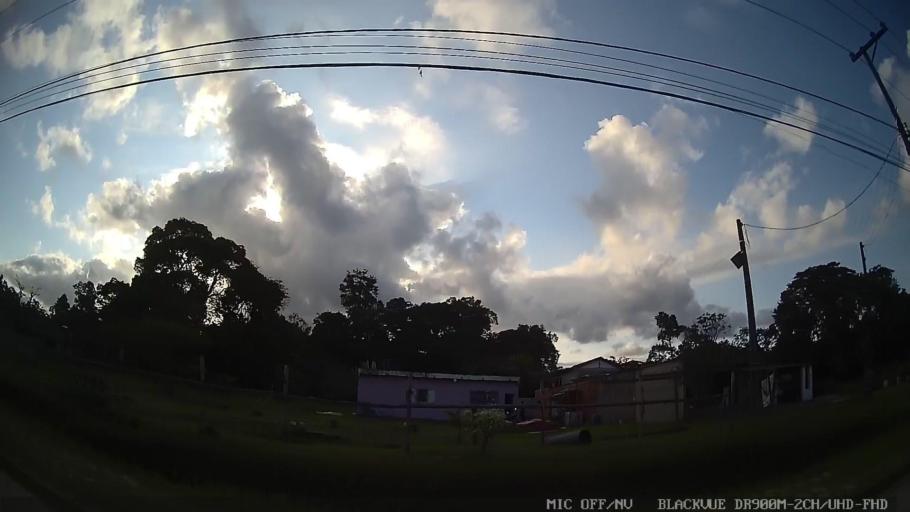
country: BR
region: Sao Paulo
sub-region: Itanhaem
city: Itanhaem
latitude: -24.1654
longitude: -46.8378
